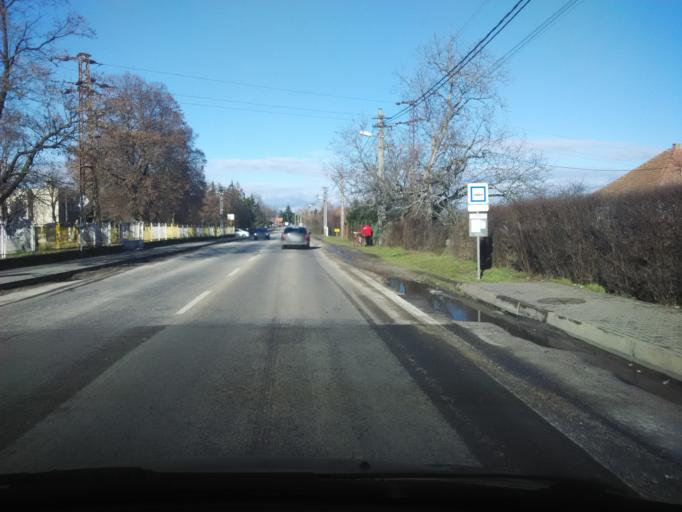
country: SK
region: Nitriansky
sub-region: Okres Nitra
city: Nitra
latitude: 48.2344
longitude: 18.1261
